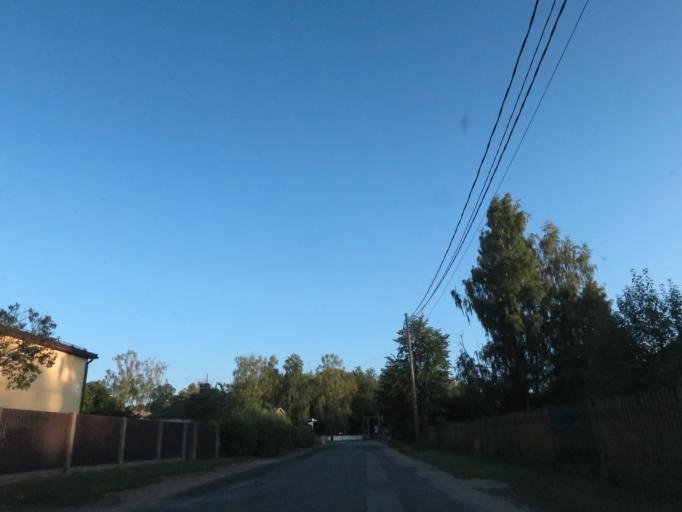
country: LV
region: Sigulda
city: Sigulda
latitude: 57.1674
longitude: 24.8616
